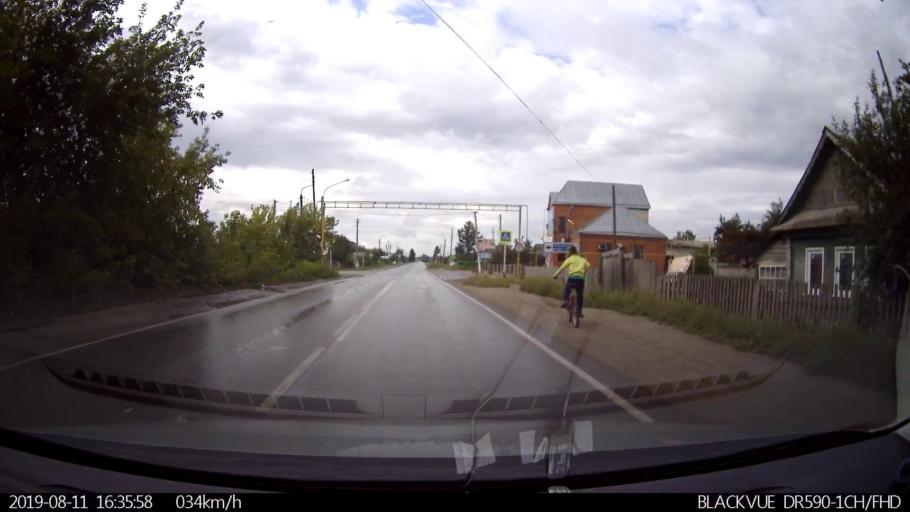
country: RU
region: Ulyanovsk
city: Mayna
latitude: 54.1167
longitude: 47.6141
